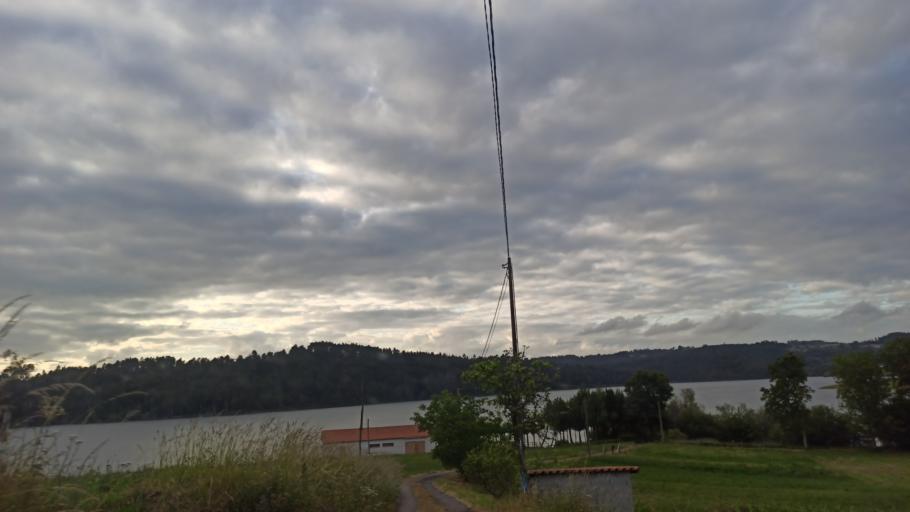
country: ES
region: Galicia
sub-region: Provincia da Coruna
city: Santiso
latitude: 42.8348
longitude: -8.1231
